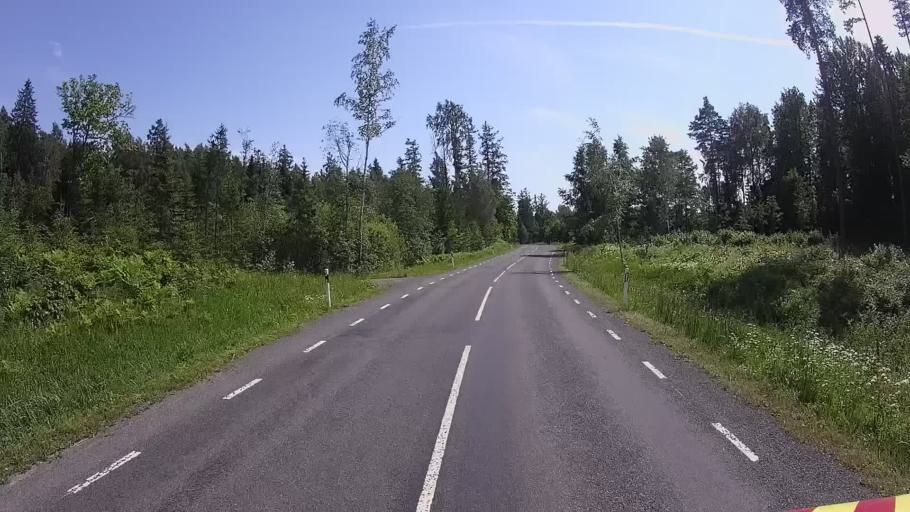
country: EE
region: Viljandimaa
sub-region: Karksi vald
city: Karksi-Nuia
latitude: 58.0811
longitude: 25.5599
